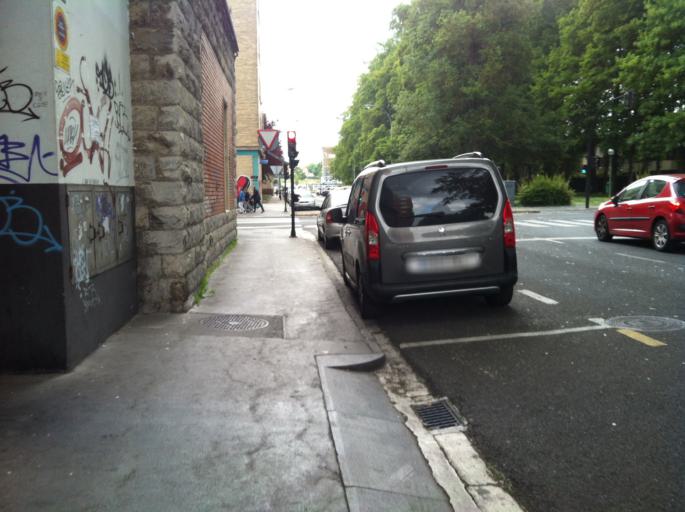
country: ES
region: Basque Country
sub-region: Provincia de Alava
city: Gasteiz / Vitoria
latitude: 42.8370
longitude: -2.6723
